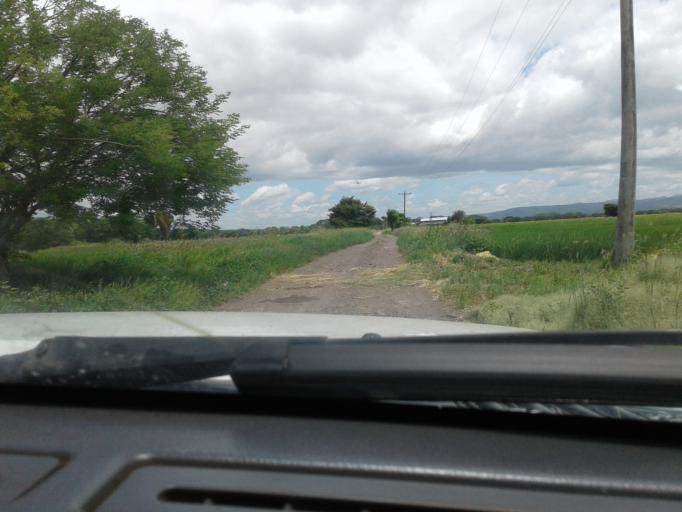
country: NI
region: Matagalpa
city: Ciudad Dario
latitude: 12.8366
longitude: -86.1251
